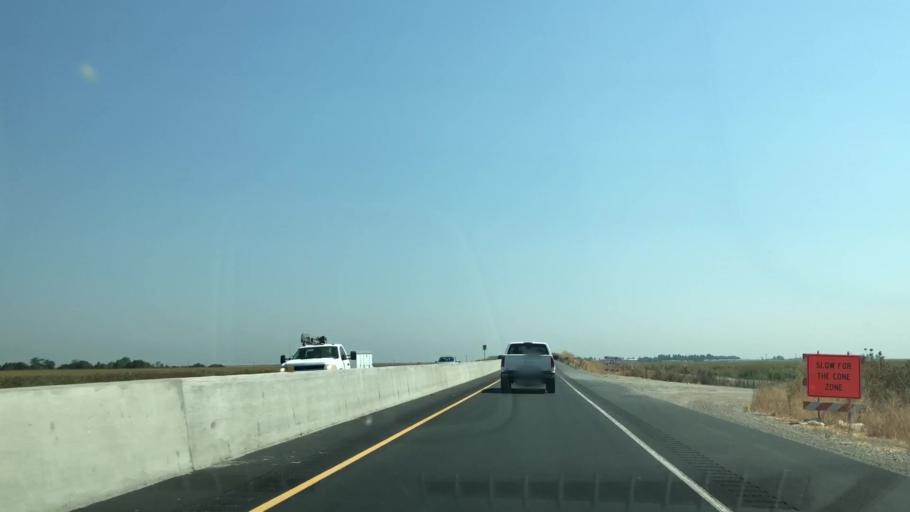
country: US
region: California
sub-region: Sacramento County
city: Walnut Grove
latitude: 38.1132
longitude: -121.5389
